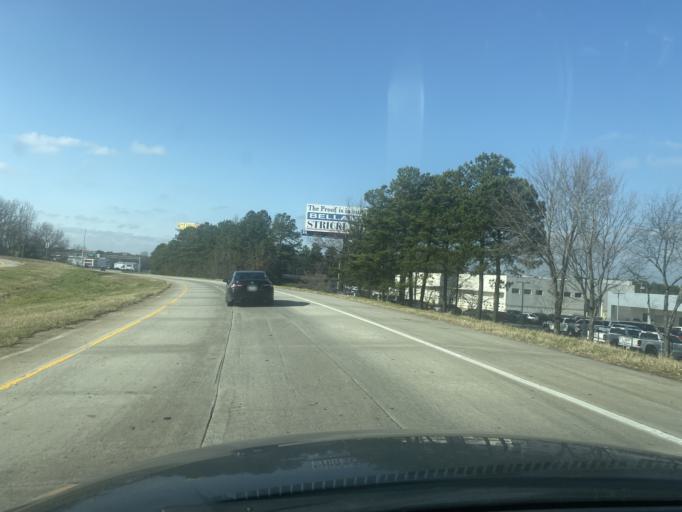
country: US
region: Georgia
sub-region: Henry County
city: McDonough
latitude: 33.4134
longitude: -84.1614
